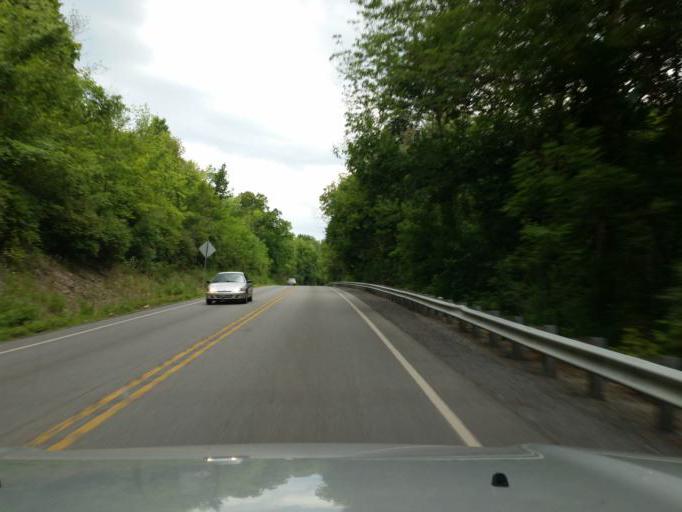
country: US
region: Pennsylvania
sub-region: Blair County
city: Greenwood
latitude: 40.5338
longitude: -78.3761
